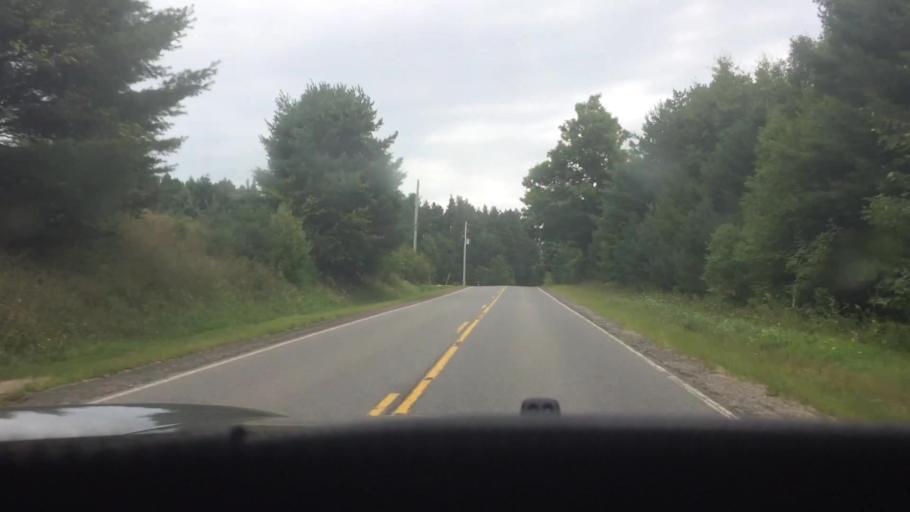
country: US
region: New York
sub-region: St. Lawrence County
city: Hannawa Falls
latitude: 44.5959
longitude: -74.8880
